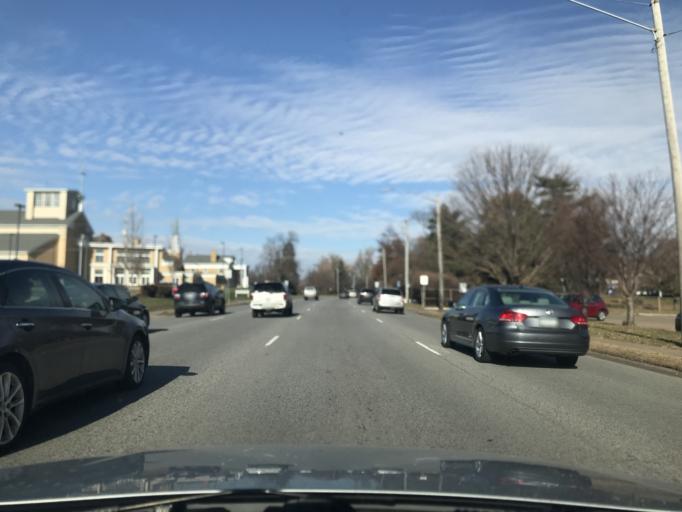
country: US
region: Iowa
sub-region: Scott County
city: Davenport
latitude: 41.5400
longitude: -90.5740
